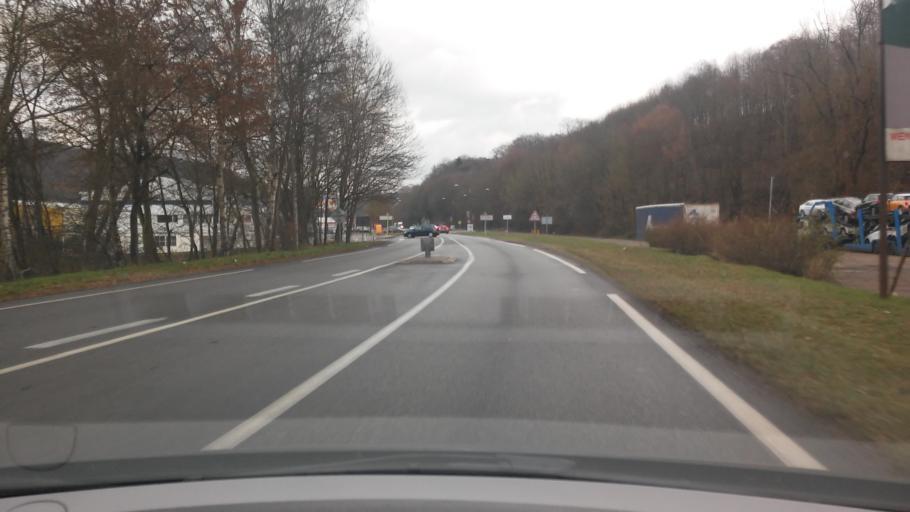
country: FR
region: Lorraine
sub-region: Departement de la Moselle
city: Saint-Avold
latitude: 49.1088
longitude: 6.7325
